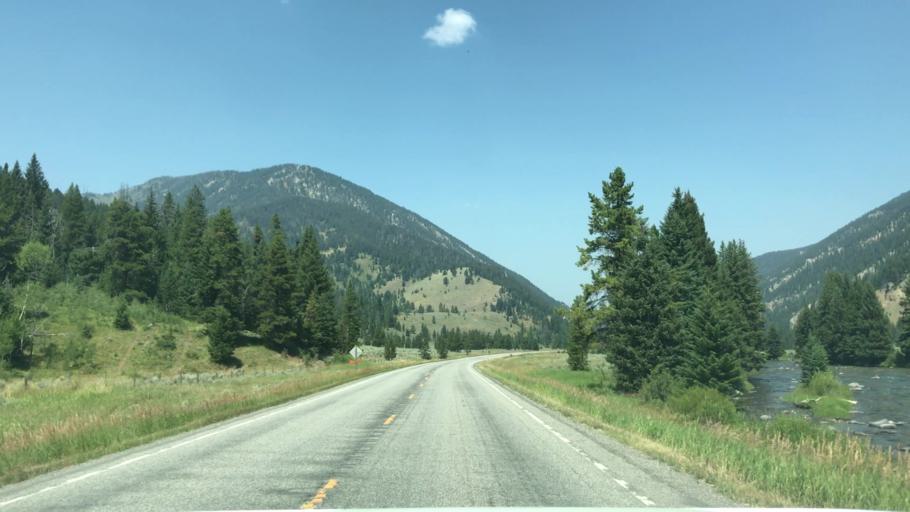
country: US
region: Montana
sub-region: Gallatin County
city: Big Sky
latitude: 45.1025
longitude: -111.2197
